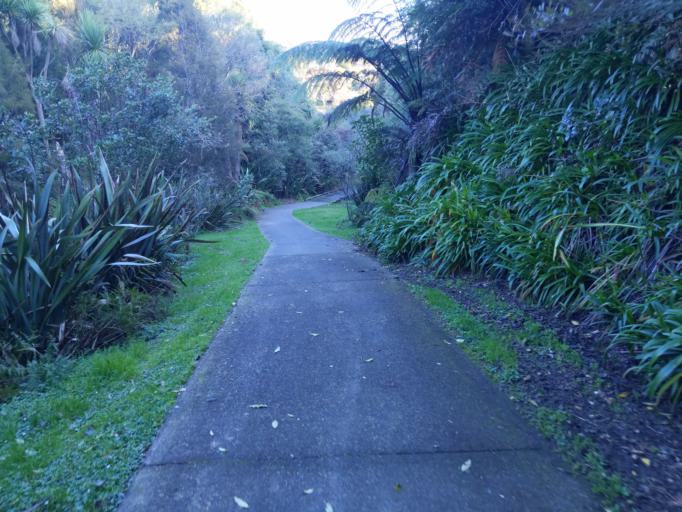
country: NZ
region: Waikato
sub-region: Hamilton City
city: Hamilton
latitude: -37.7400
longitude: 175.2766
